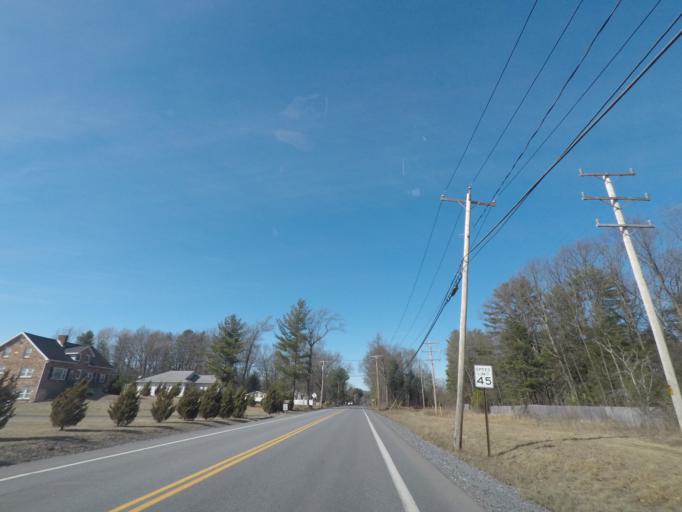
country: US
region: New York
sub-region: Saratoga County
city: Milton
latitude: 43.0591
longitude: -73.8505
